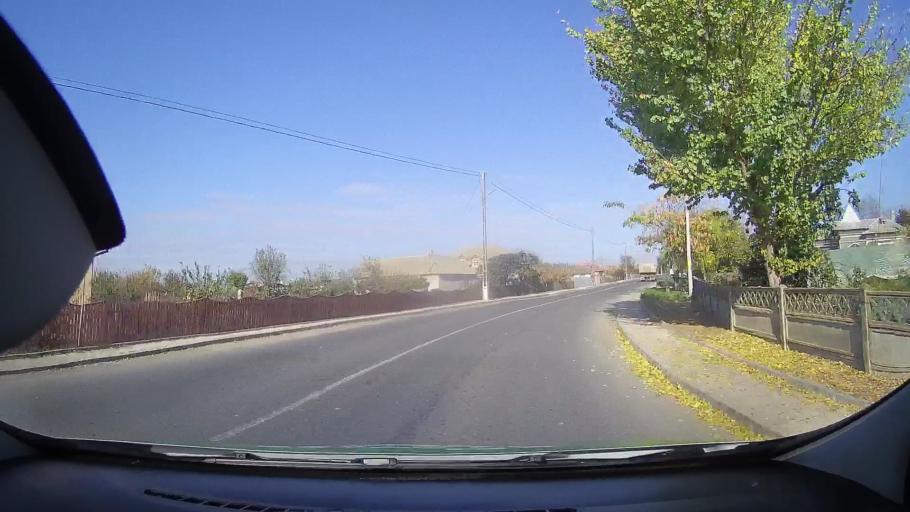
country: RO
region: Tulcea
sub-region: Comuna Mahmudia
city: Mahmudia
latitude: 45.0090
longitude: 29.0553
